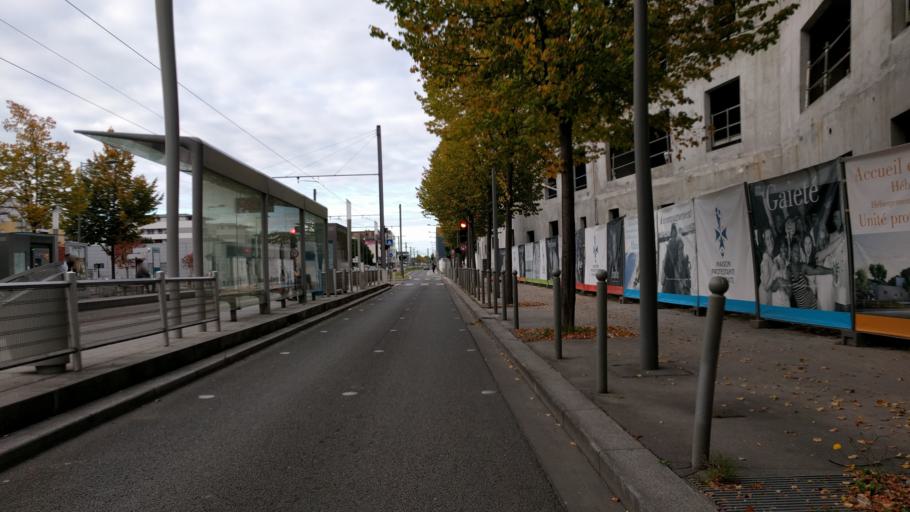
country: FR
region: Aquitaine
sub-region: Departement de la Gironde
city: Le Bouscat
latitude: 44.8622
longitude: -0.5752
